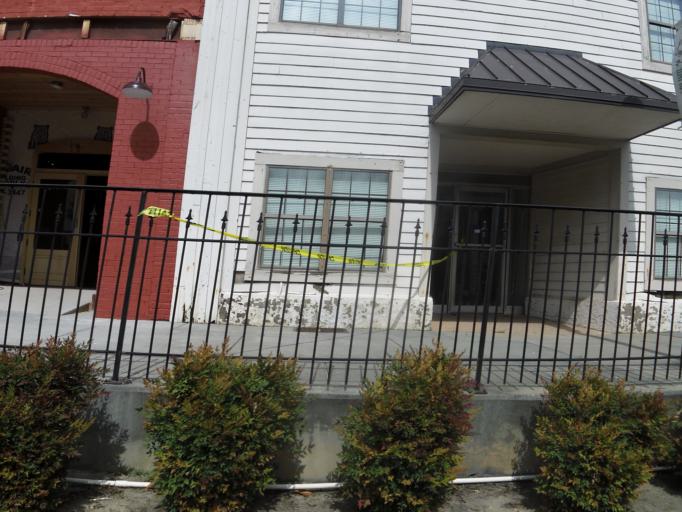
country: US
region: Georgia
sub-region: McDuffie County
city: Thomson
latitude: 33.4664
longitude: -82.5026
